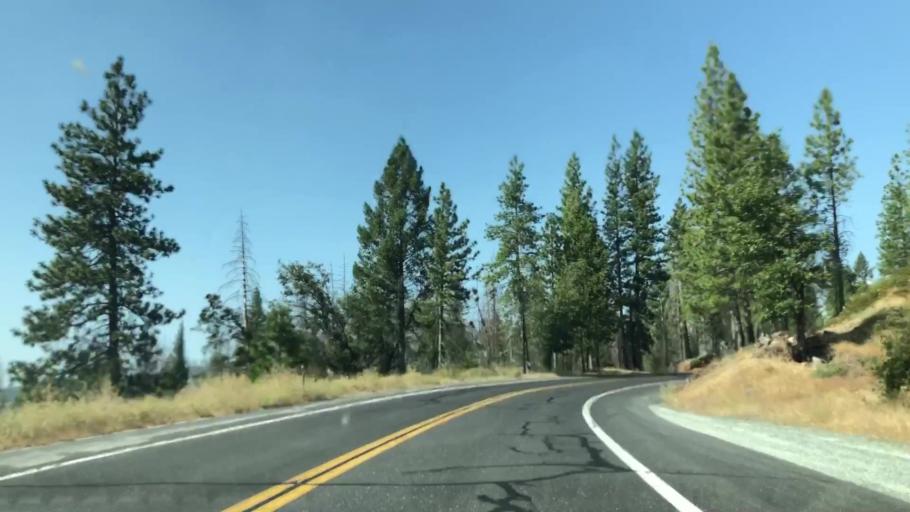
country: US
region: California
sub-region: Mariposa County
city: Midpines
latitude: 37.8126
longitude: -119.8998
